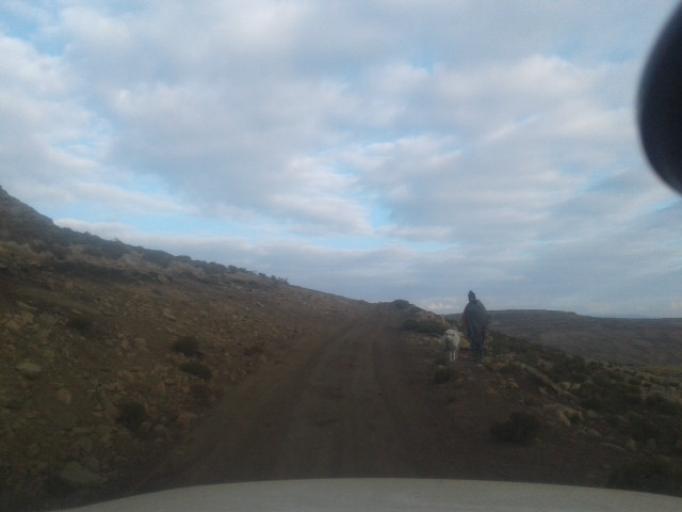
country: LS
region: Thaba-Tseka
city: Thaba-Tseka
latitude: -29.4146
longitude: 28.2711
